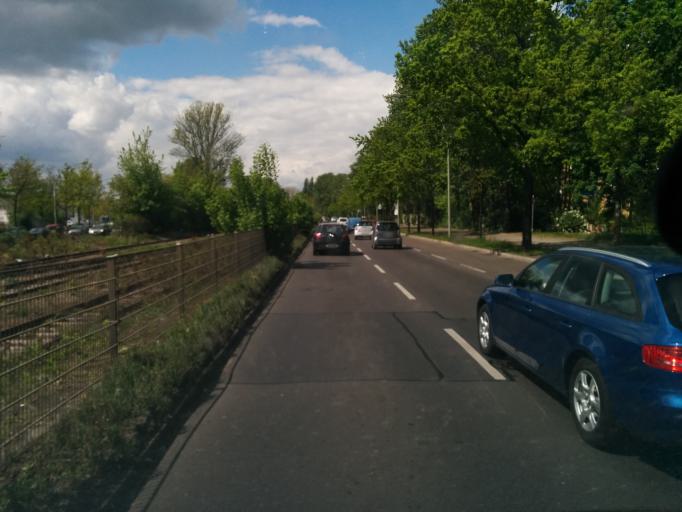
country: DE
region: Berlin
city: Haselhorst
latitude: 52.5391
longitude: 13.2391
